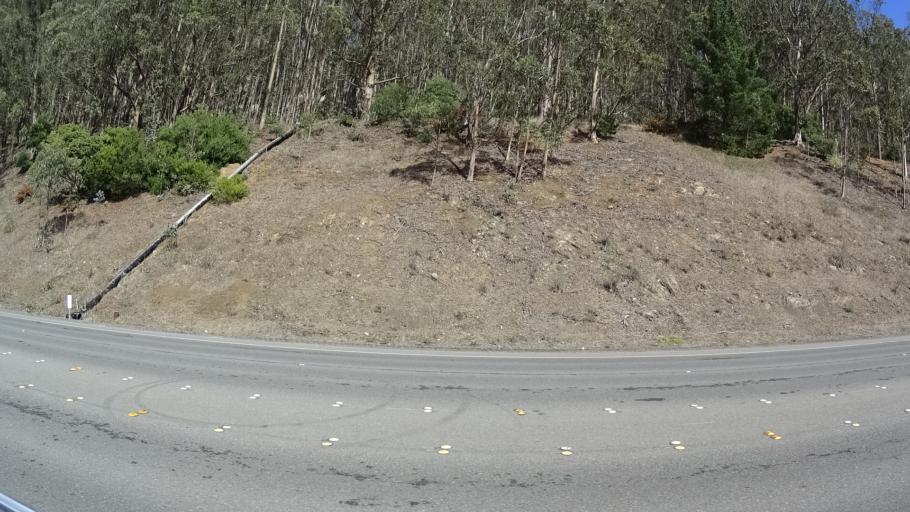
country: US
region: California
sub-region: San Mateo County
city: Daly City
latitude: 37.6995
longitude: -122.4424
